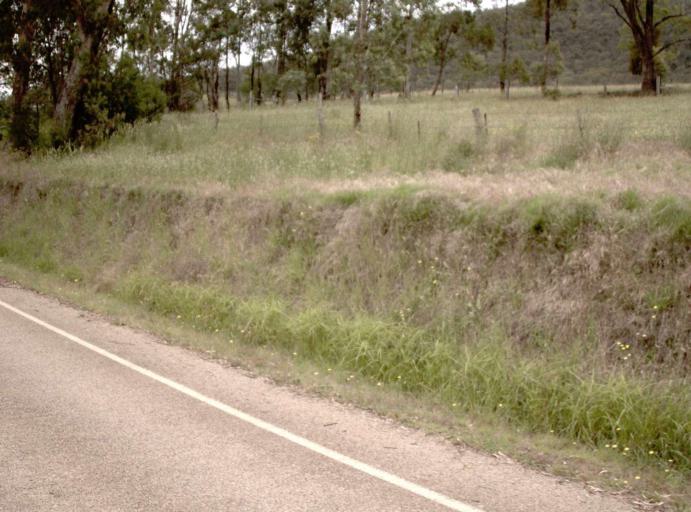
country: AU
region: Victoria
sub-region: East Gippsland
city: Bairnsdale
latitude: -37.5489
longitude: 147.1998
